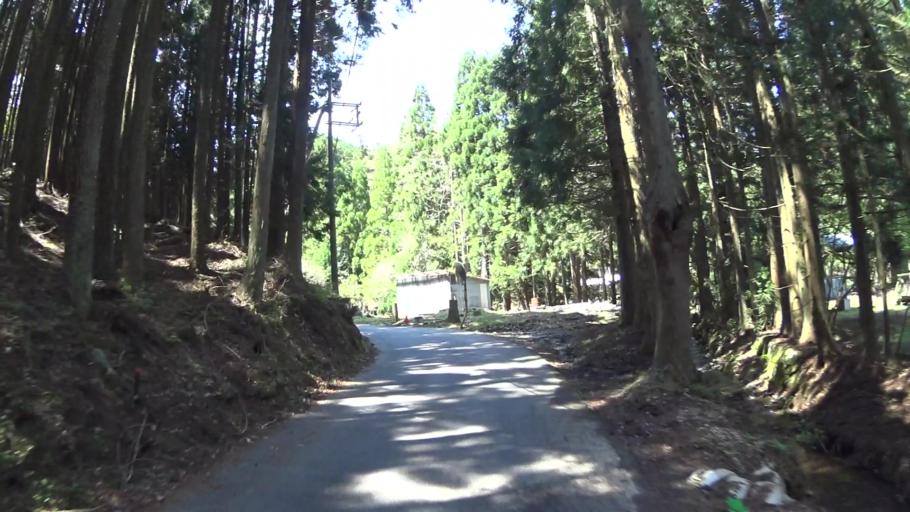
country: JP
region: Shiga Prefecture
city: Kitahama
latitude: 35.1615
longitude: 135.8019
